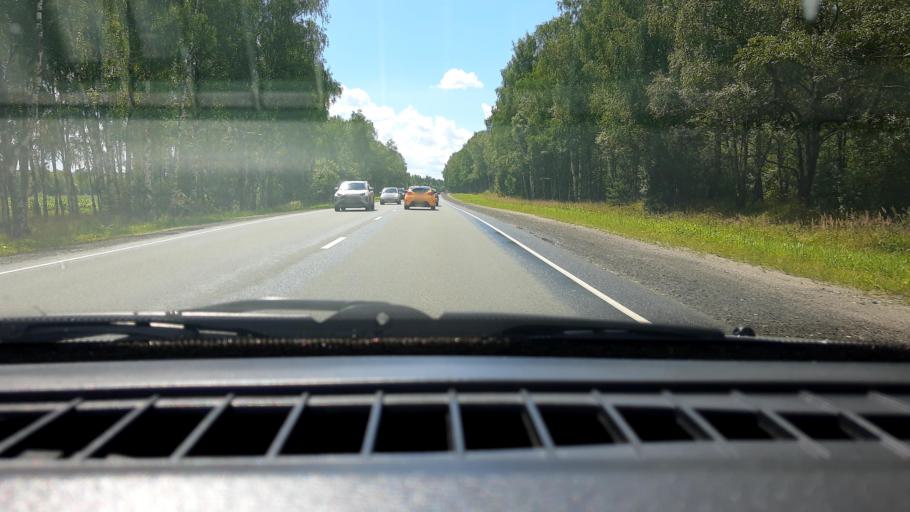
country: RU
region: Nizjnij Novgorod
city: Linda
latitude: 56.5947
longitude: 44.0378
